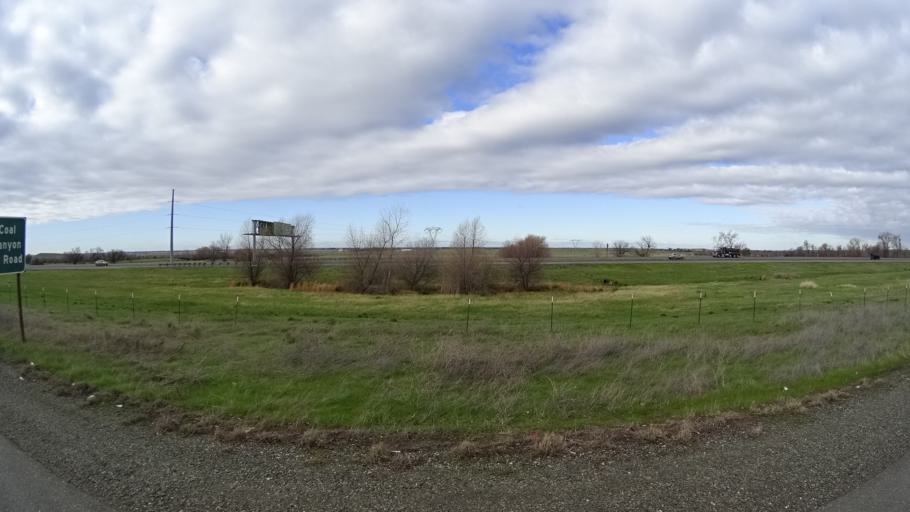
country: US
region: California
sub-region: Butte County
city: Thermalito
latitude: 39.5940
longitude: -121.6194
